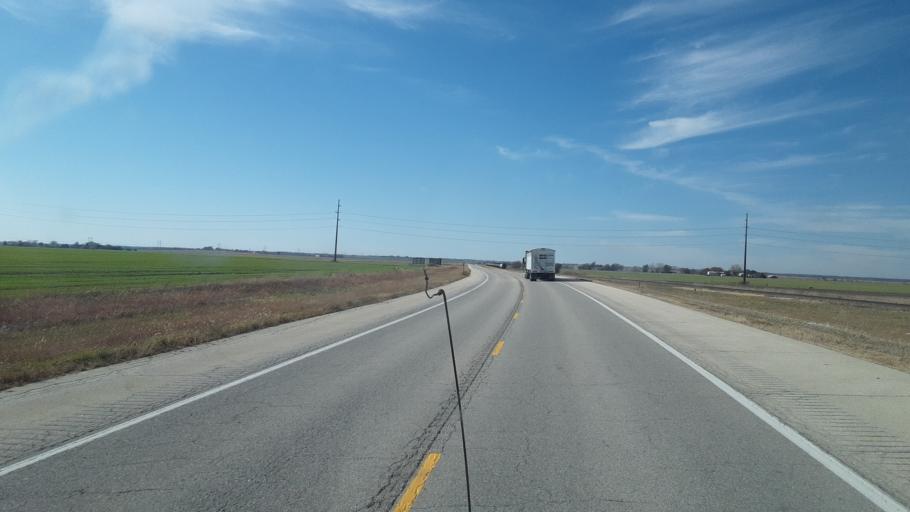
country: US
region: Kansas
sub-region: McPherson County
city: McPherson
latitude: 38.3694
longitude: -97.7086
